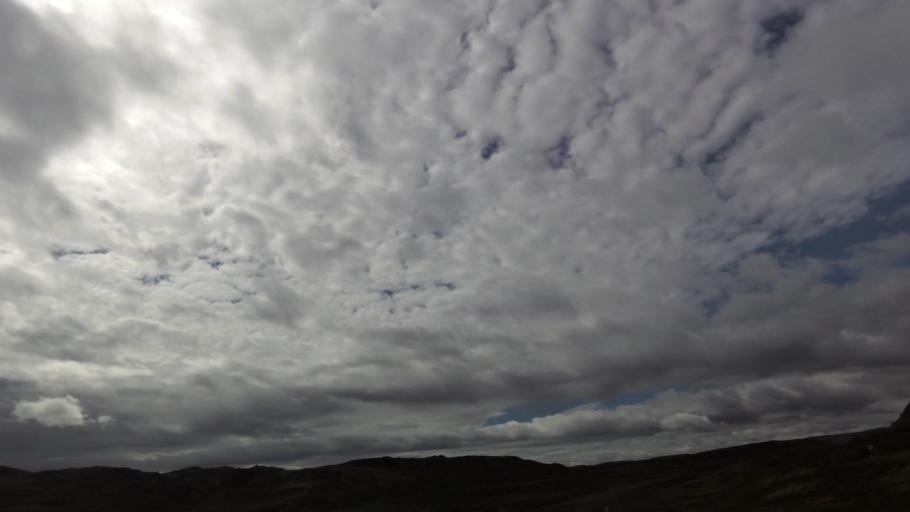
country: IS
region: West
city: Stykkisholmur
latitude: 65.5344
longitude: -22.0885
